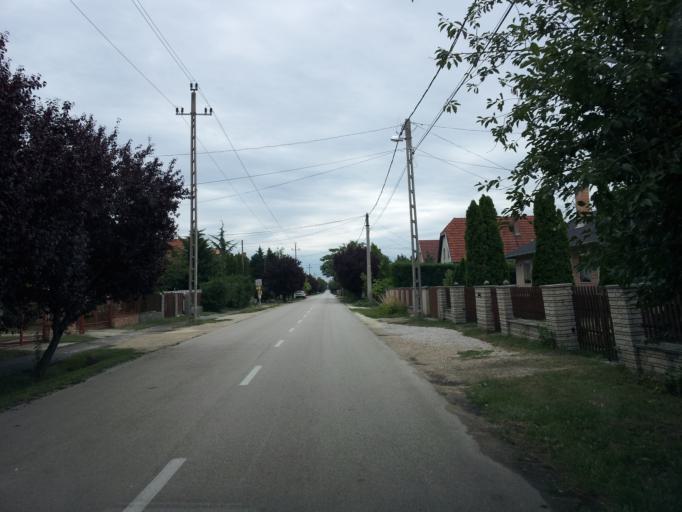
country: HU
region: Pest
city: Tarnok
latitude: 47.3771
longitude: 18.8619
